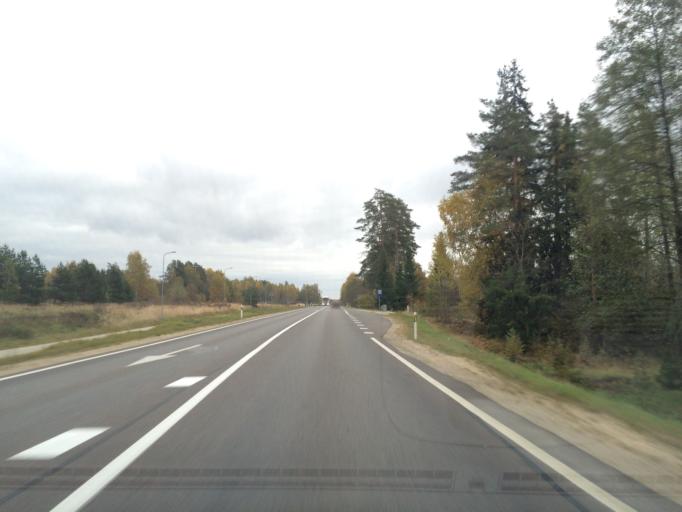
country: LV
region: Jekabpils Rajons
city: Jekabpils
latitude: 56.5406
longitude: 26.0676
